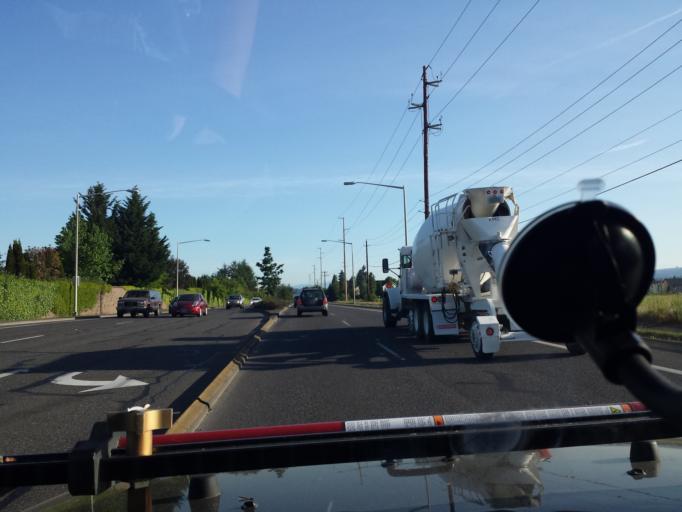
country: US
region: Washington
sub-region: Clark County
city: Mill Plain
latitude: 45.6509
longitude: -122.5060
